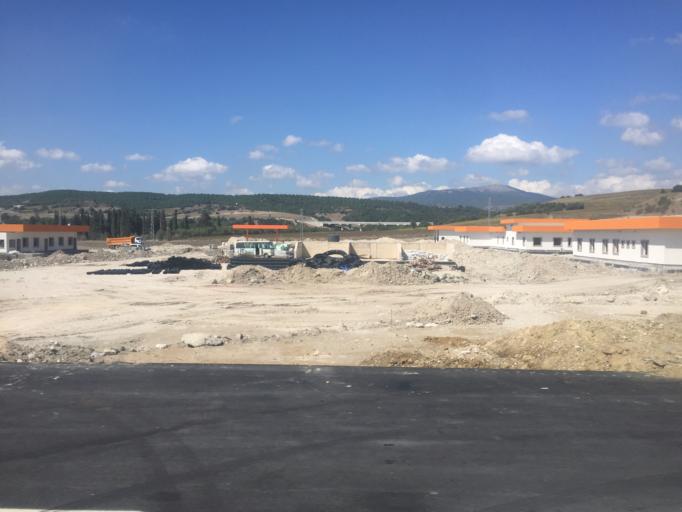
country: TR
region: Balikesir
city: Susurluk
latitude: 39.9610
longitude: 28.1650
